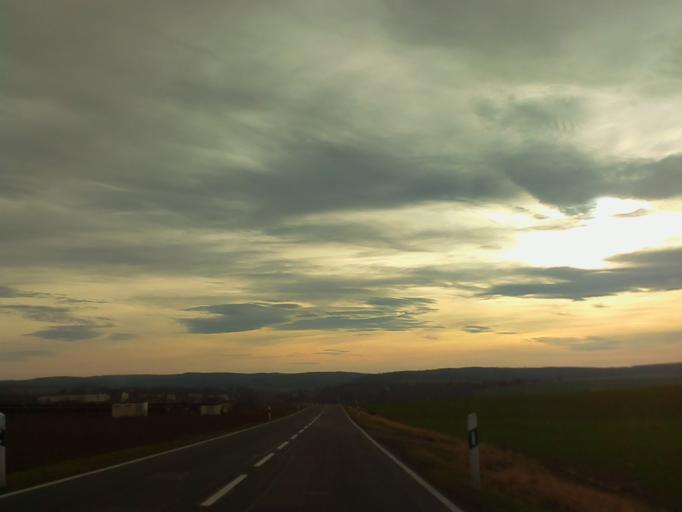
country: DE
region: Thuringia
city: Ruttersdorf-Lotschen
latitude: 50.8794
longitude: 11.7298
